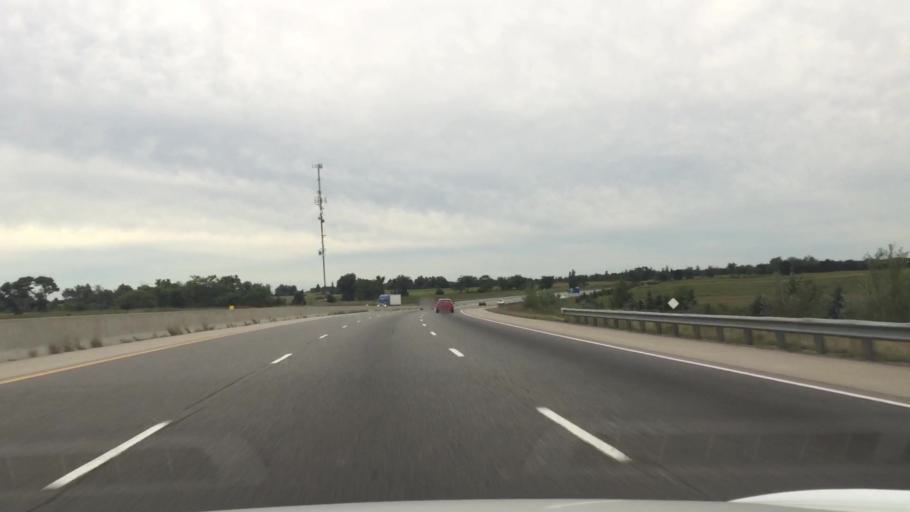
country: CA
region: Ontario
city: Kitchener
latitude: 43.2432
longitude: -80.5736
